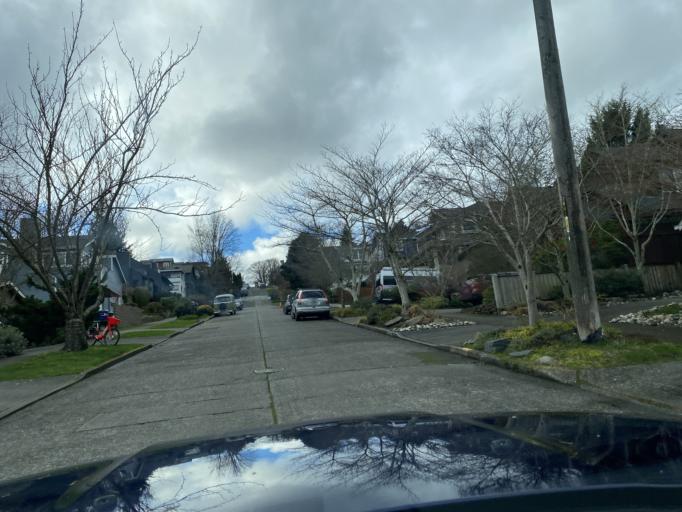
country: US
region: Washington
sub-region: King County
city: Seattle
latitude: 47.6259
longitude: -122.2974
